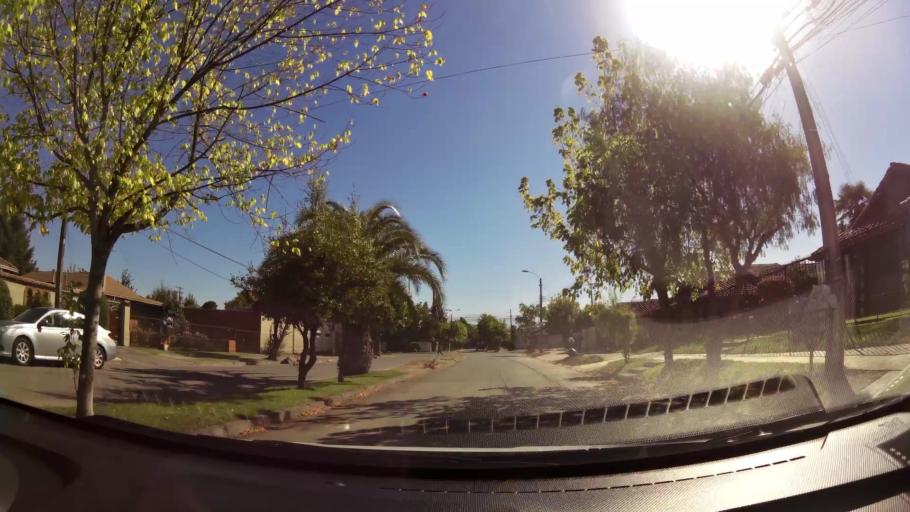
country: CL
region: O'Higgins
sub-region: Provincia de Cachapoal
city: Rancagua
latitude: -34.1819
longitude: -70.7097
